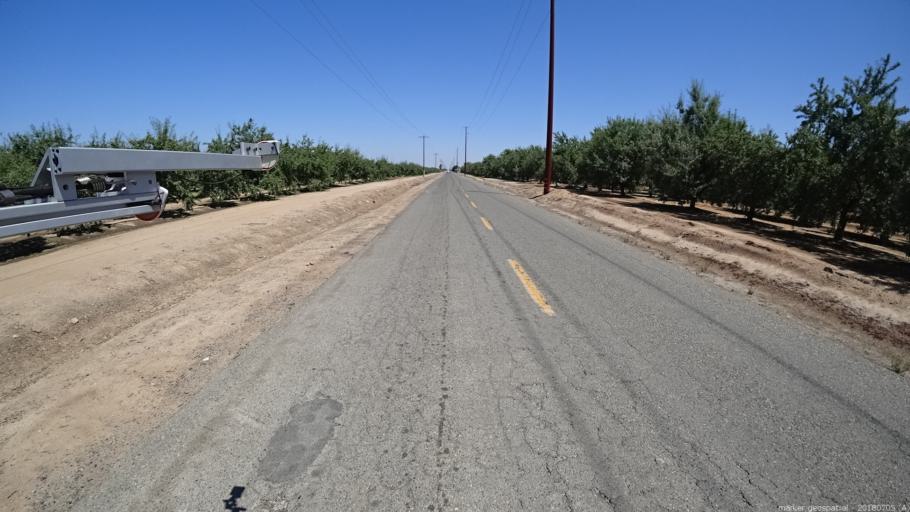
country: US
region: California
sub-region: Madera County
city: Chowchilla
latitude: 37.1447
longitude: -120.2021
